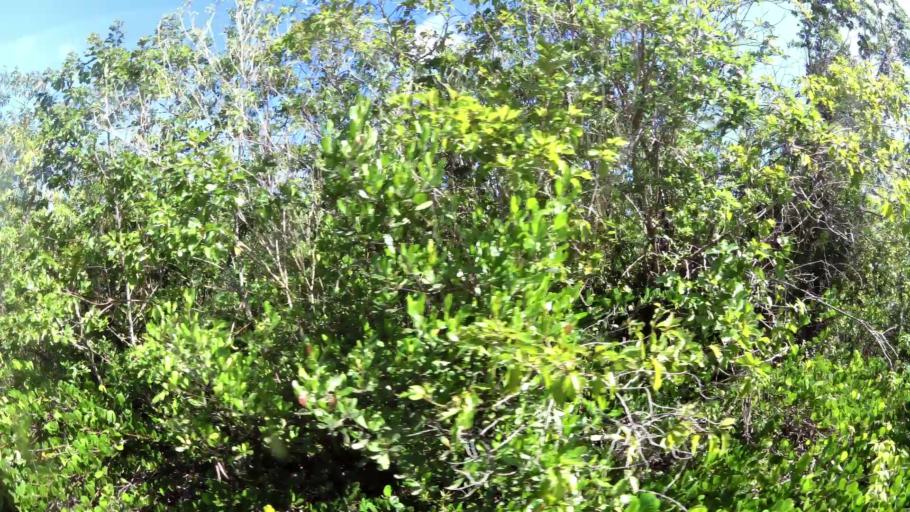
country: AG
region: Barbuda
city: Codrington
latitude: 17.5950
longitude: -61.8286
